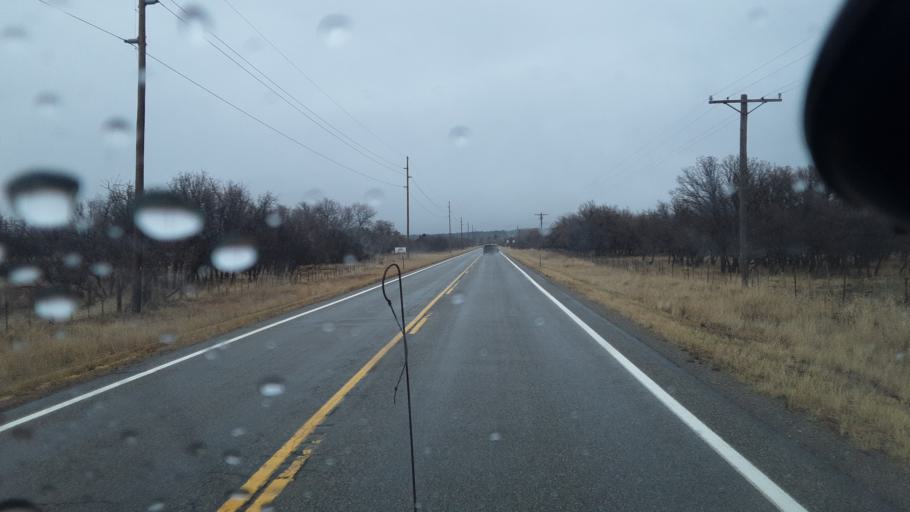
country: US
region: Colorado
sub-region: La Plata County
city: Durango
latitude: 37.2329
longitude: -108.0463
